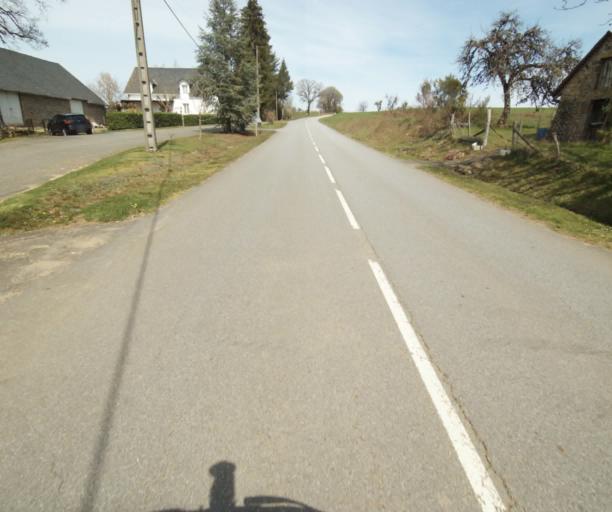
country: FR
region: Limousin
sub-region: Departement de la Correze
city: Correze
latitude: 45.3825
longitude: 1.8048
